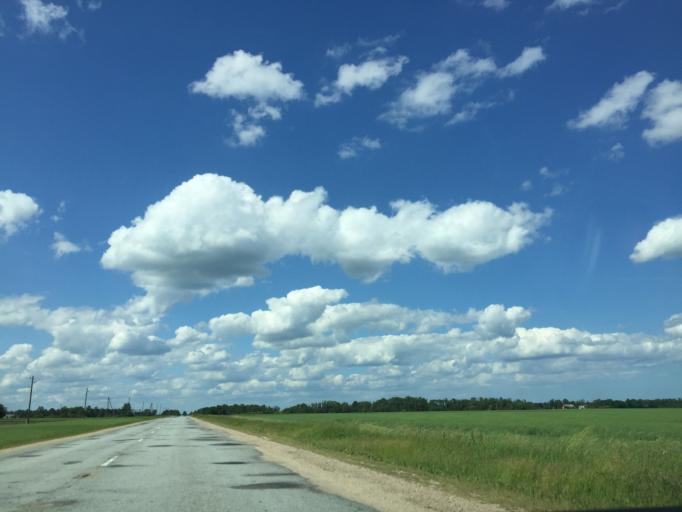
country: LV
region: Engure
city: Smarde
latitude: 56.8043
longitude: 23.3618
